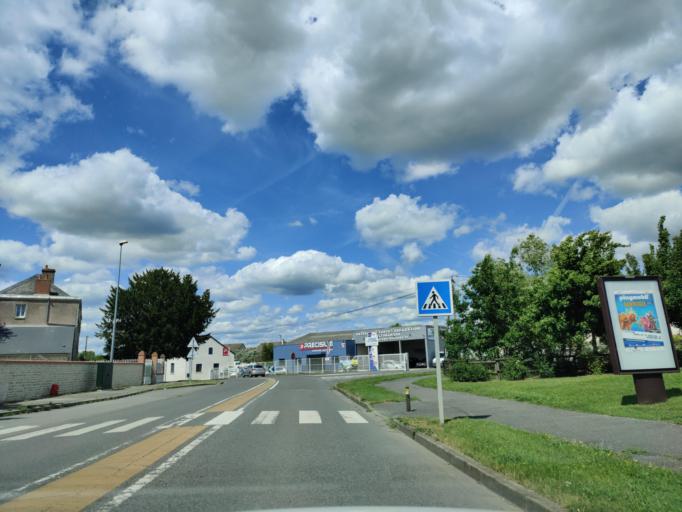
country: FR
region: Centre
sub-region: Departement du Loiret
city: Pithiviers
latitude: 48.1620
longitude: 2.2586
